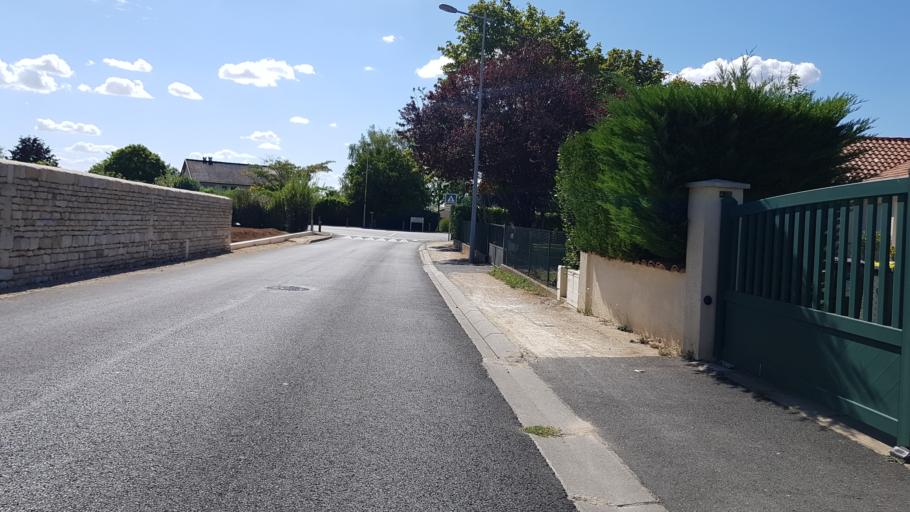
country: FR
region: Poitou-Charentes
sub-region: Departement des Deux-Sevres
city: Vouille
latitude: 46.3112
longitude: -0.3627
